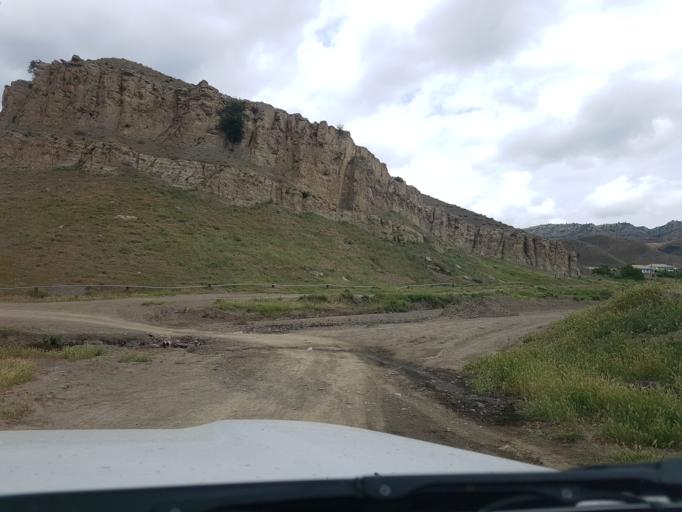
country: TM
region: Ahal
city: Baharly
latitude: 38.2015
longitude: 57.0044
